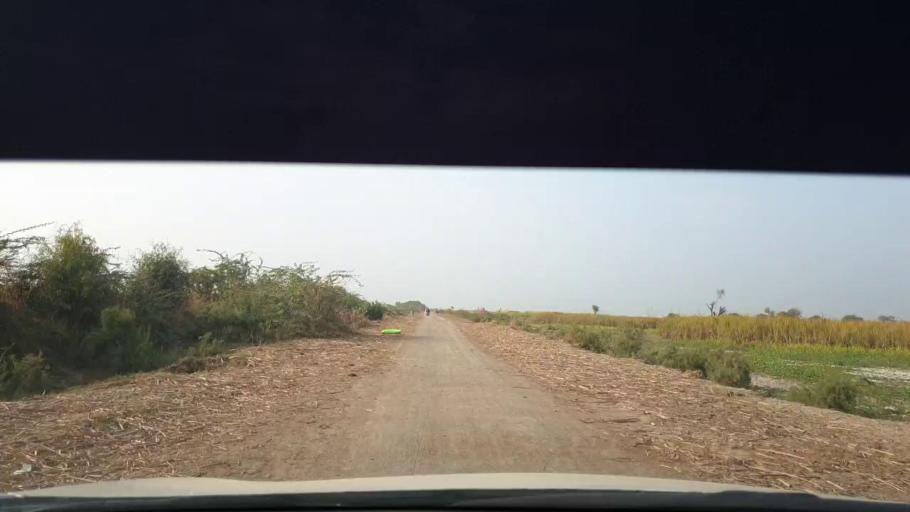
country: PK
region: Sindh
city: Berani
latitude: 25.7458
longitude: 68.9483
